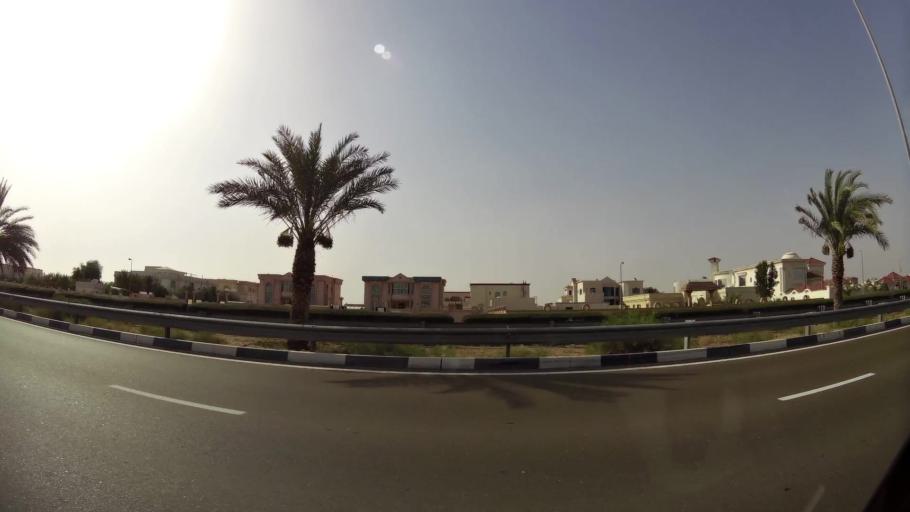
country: AE
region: Abu Dhabi
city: Al Ain
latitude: 24.2237
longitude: 55.6540
